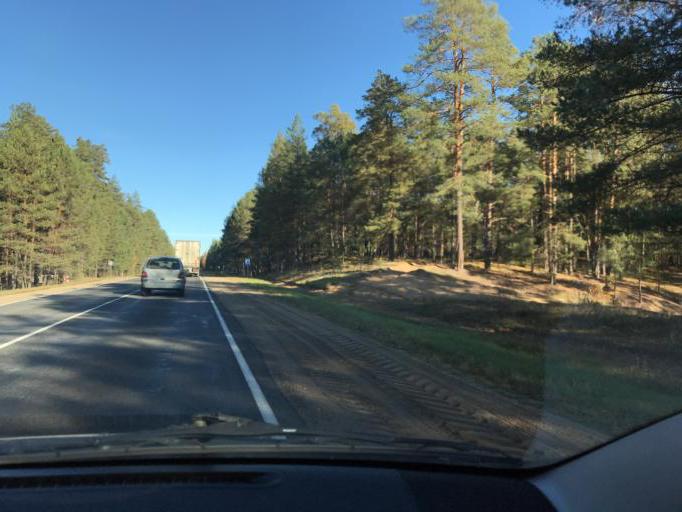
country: BY
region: Vitebsk
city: Polatsk
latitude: 55.3450
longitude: 28.7965
